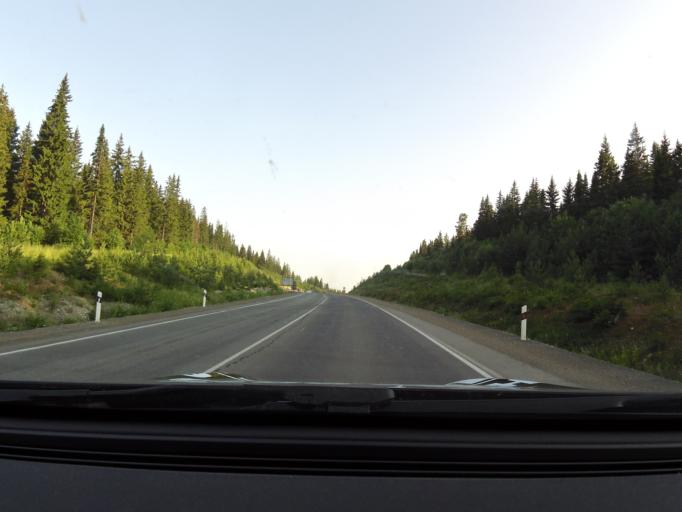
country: RU
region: Sverdlovsk
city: Nizhniye Sergi
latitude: 56.6657
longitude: 59.2683
